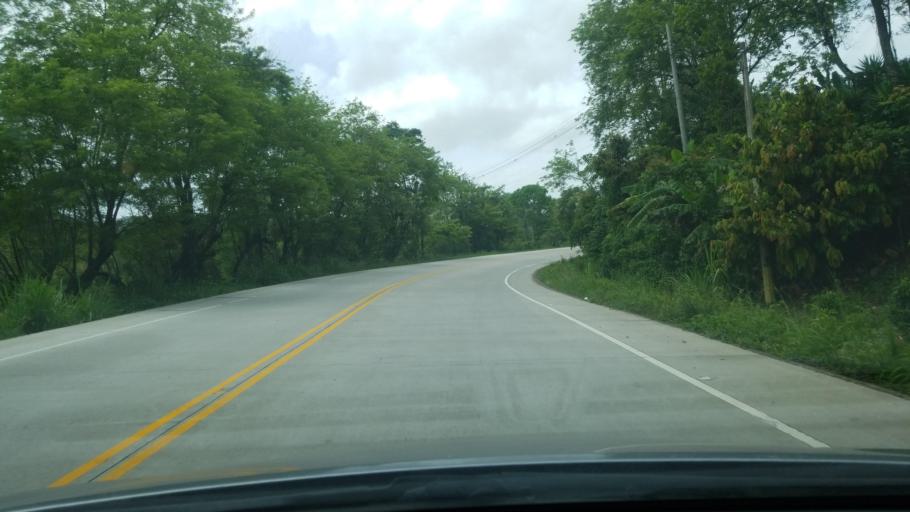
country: HN
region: Copan
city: San Juan de Planes
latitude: 14.9377
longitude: -88.7649
